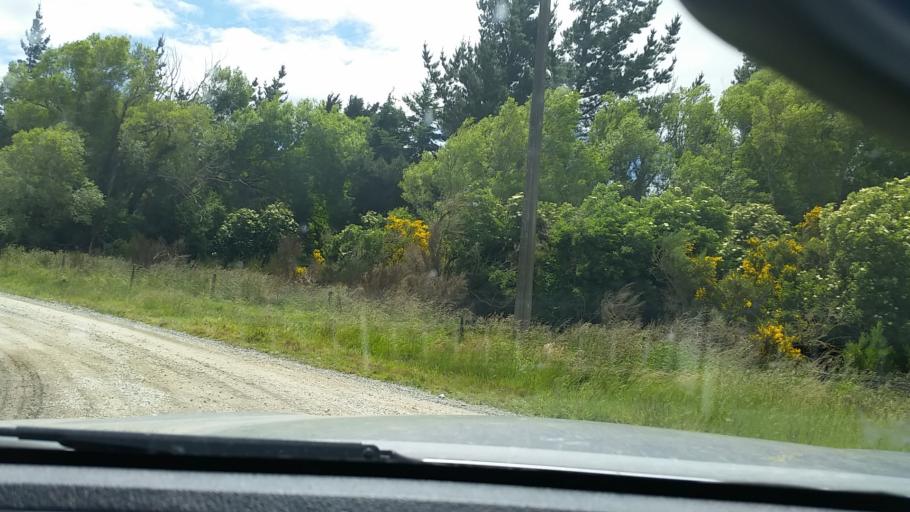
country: NZ
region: Southland
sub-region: Southland District
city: Winton
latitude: -45.7626
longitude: 168.4935
